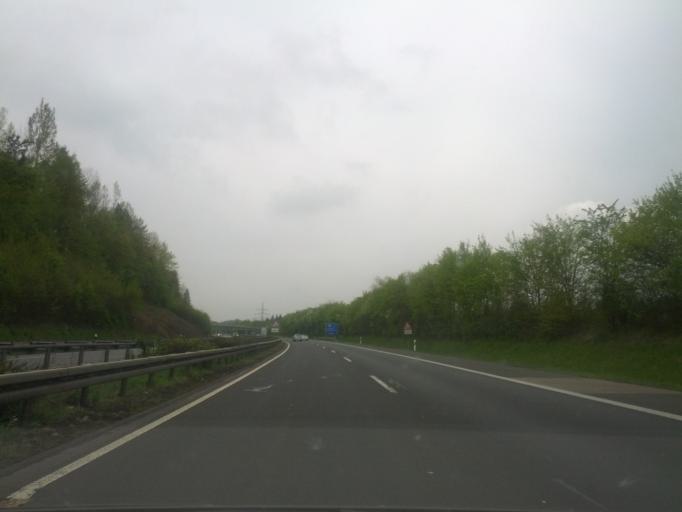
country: DE
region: Hesse
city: Lollar
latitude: 50.6347
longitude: 8.7231
